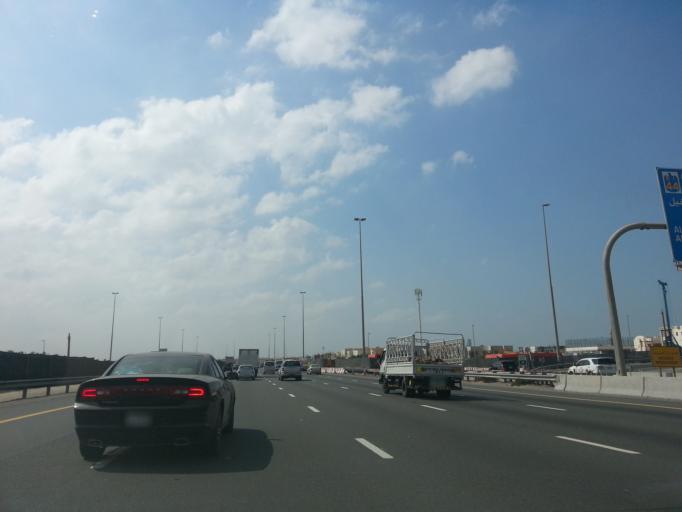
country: AE
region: Dubai
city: Dubai
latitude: 25.1689
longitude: 55.2676
